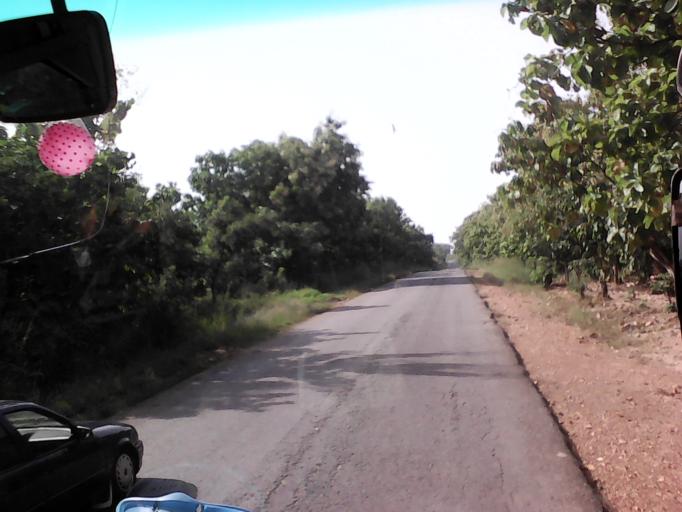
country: TG
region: Centrale
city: Sokode
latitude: 9.1260
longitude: 1.1472
